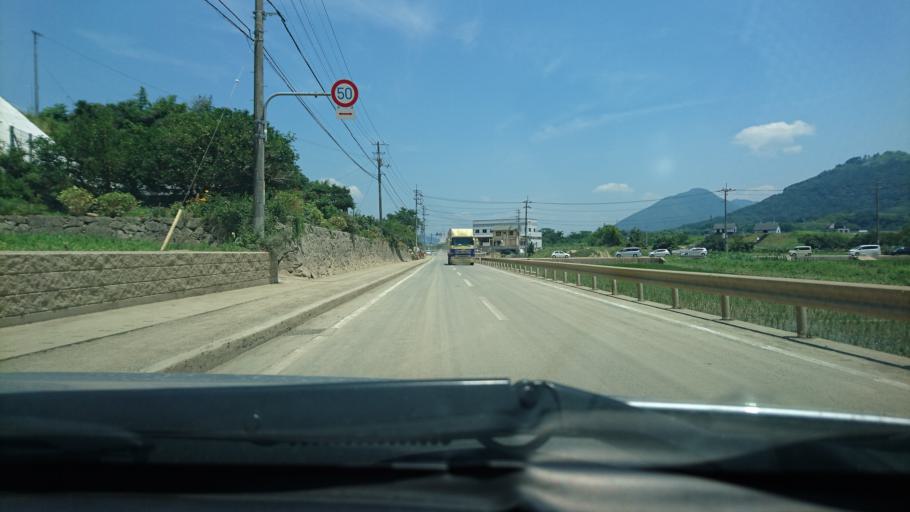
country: JP
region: Ehime
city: Ozu
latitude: 33.5115
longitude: 132.5352
